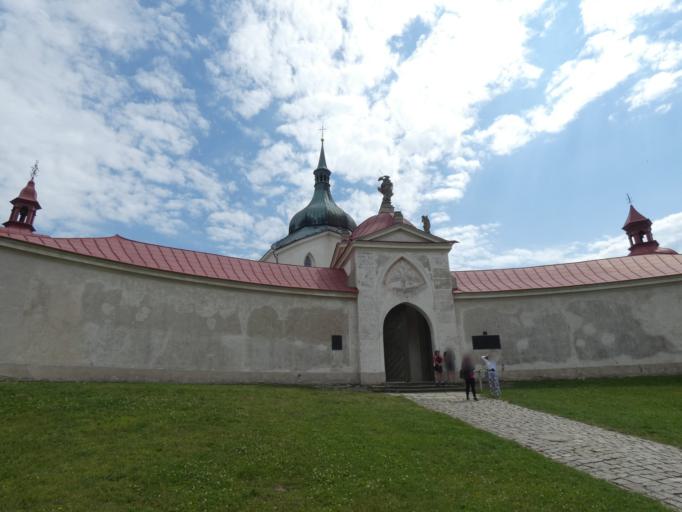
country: CZ
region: Vysocina
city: Zd'ar nad Sazavou Druhy
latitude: 49.5802
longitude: 15.9411
